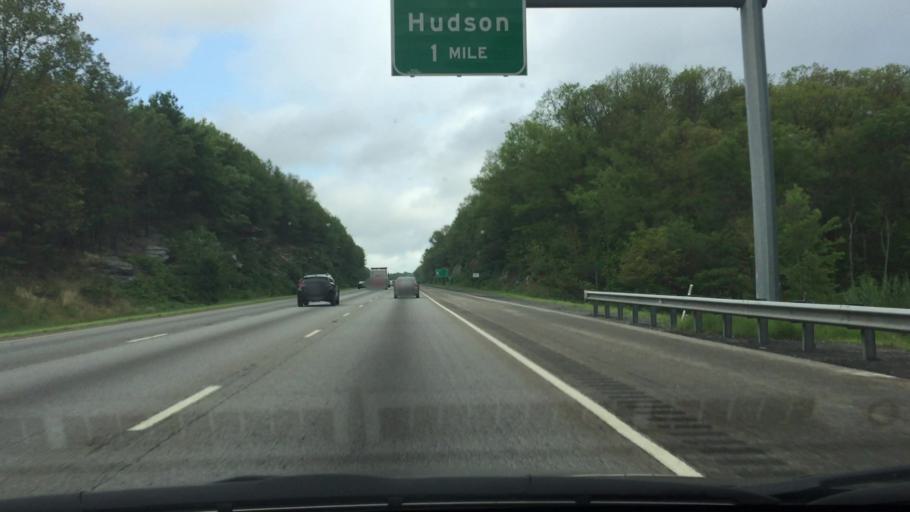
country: US
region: Massachusetts
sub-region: Middlesex County
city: Hudson
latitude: 42.3783
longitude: -71.5994
